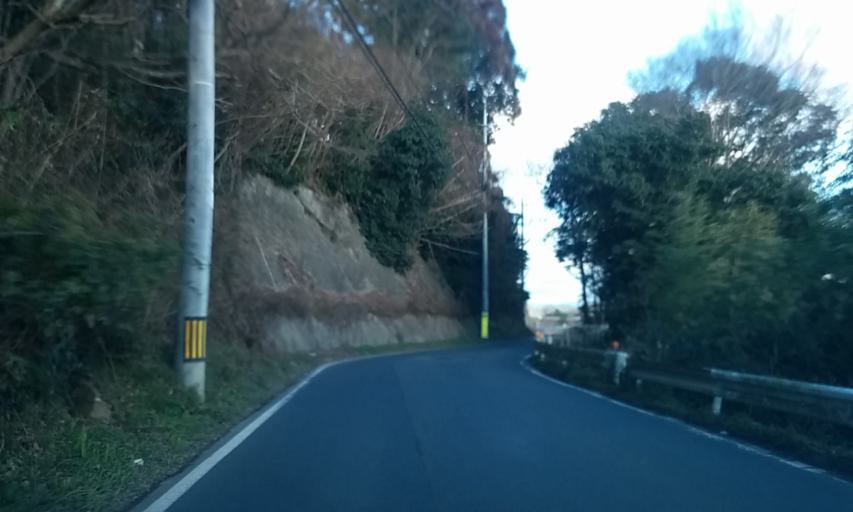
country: JP
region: Kyoto
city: Fukuchiyama
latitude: 35.3083
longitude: 135.1518
